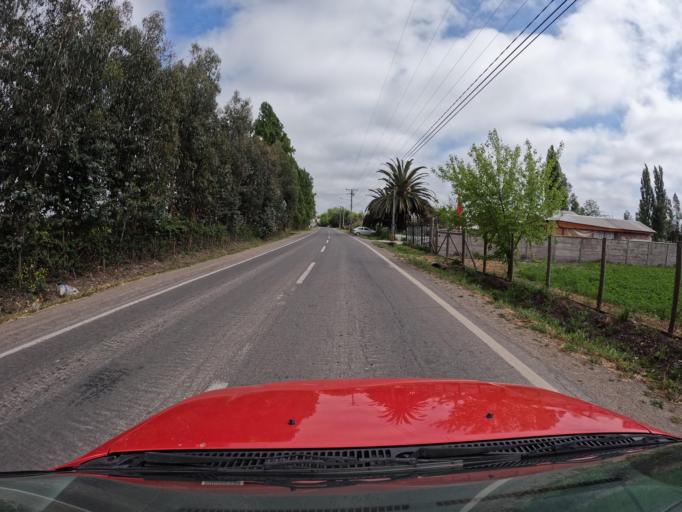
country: CL
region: O'Higgins
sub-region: Provincia de Colchagua
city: Santa Cruz
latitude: -34.6848
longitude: -71.3313
